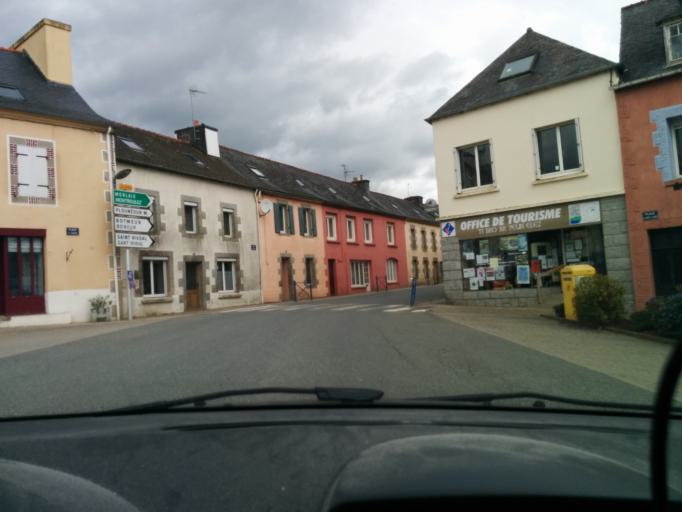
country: FR
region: Brittany
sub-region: Departement du Finistere
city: Brasparts
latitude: 48.3021
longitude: -3.9560
